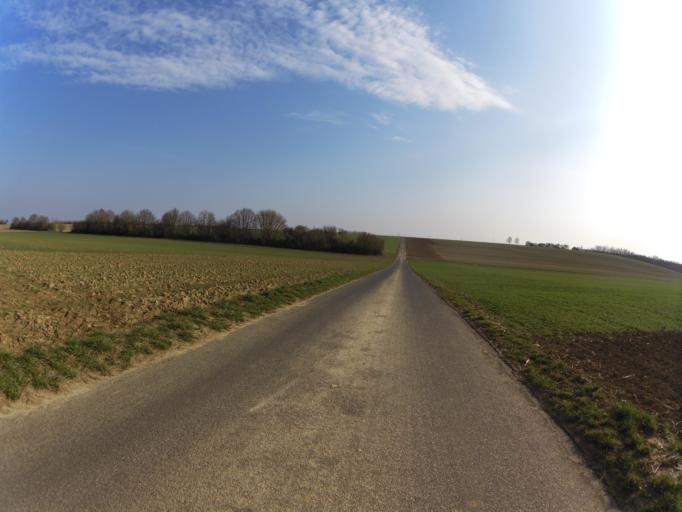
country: DE
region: Bavaria
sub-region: Regierungsbezirk Unterfranken
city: Sulzdorf
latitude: 49.6439
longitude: 9.9236
